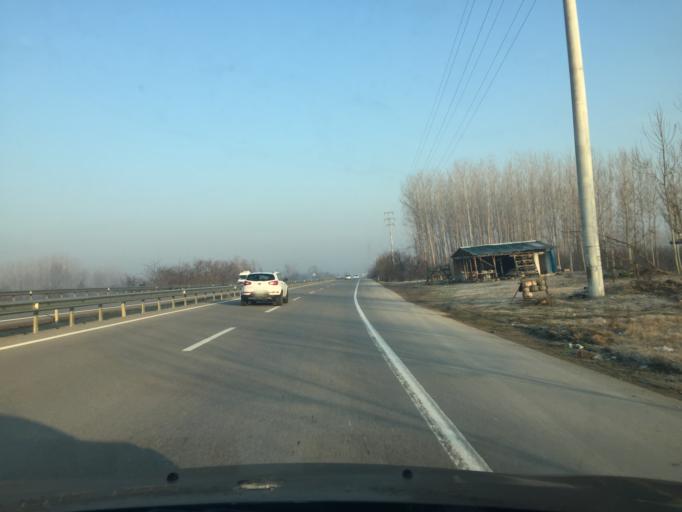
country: TR
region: Sakarya
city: Akyazi
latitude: 40.6816
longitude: 30.5772
